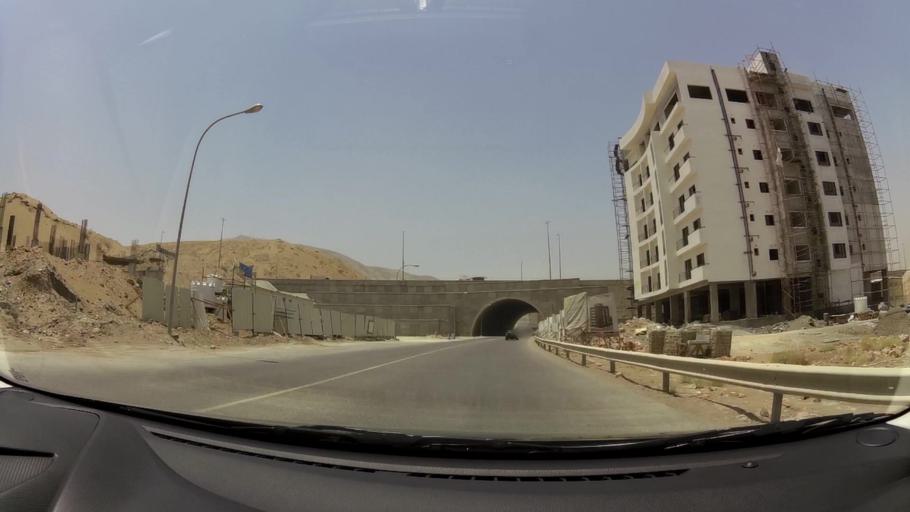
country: OM
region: Muhafazat Masqat
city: Bawshar
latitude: 23.5716
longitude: 58.4158
